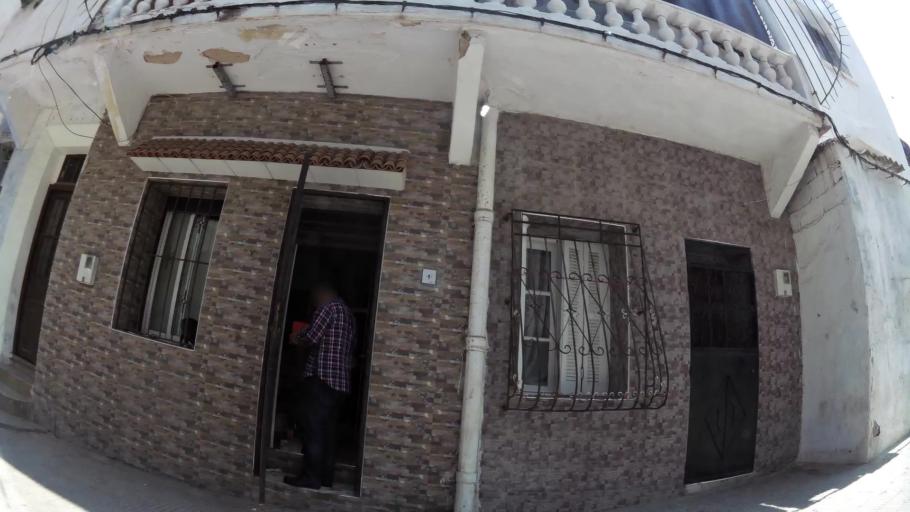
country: MA
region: Rabat-Sale-Zemmour-Zaer
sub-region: Rabat
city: Rabat
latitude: 34.0248
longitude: -6.8483
